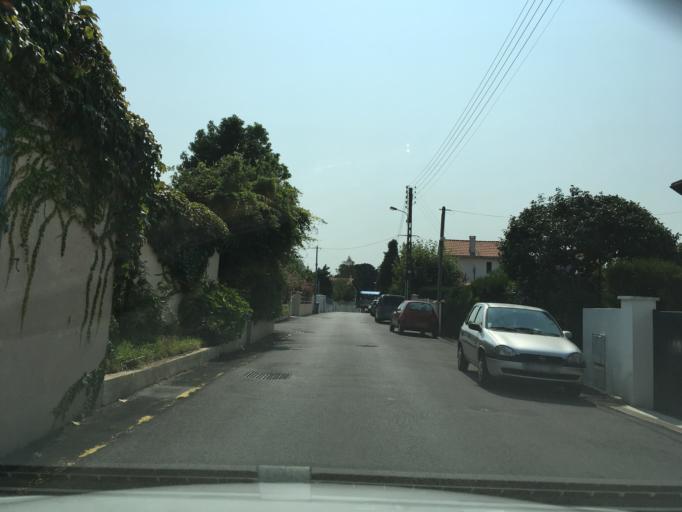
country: FR
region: Aquitaine
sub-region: Departement des Pyrenees-Atlantiques
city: Anglet
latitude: 43.4943
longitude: -1.5318
